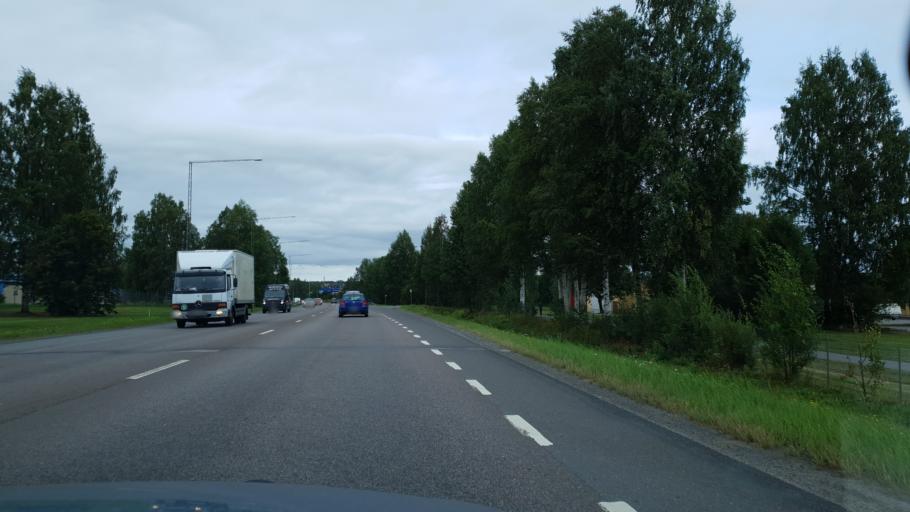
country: SE
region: Vaesterbotten
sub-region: Skelleftea Kommun
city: Skelleftea
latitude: 64.7397
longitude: 20.9642
